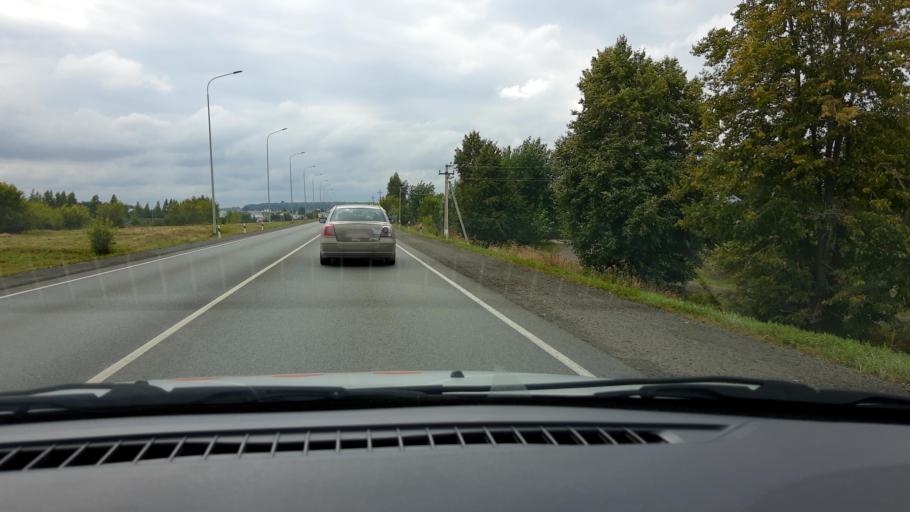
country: RU
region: Tatarstan
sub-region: Alekseyevskiy Rayon
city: Alekseyevskoye
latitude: 55.3038
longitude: 50.1317
